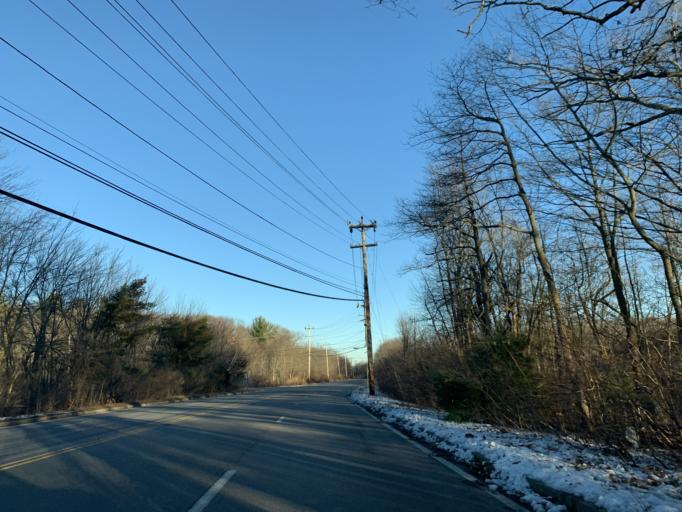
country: US
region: Rhode Island
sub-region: Kent County
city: West Warwick
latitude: 41.6667
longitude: -71.5120
